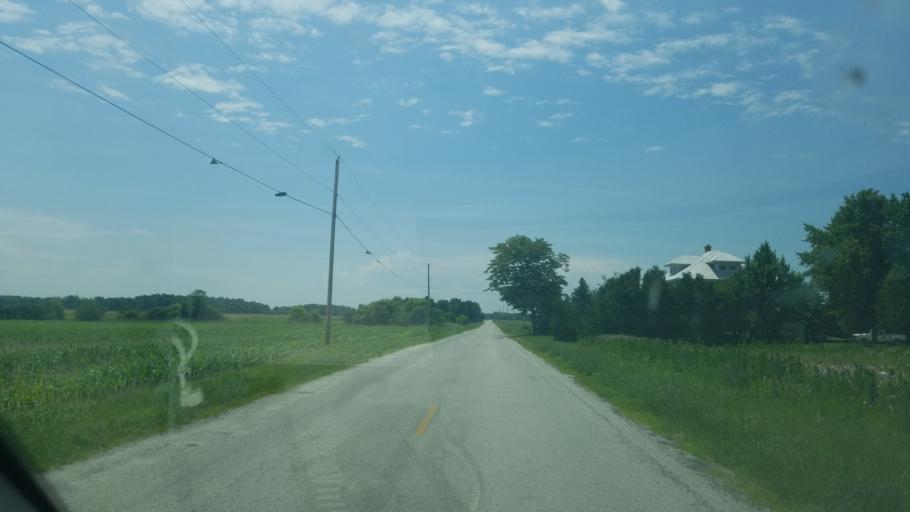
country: US
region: Ohio
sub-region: Wood County
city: North Baltimore
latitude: 41.2096
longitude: -83.5923
